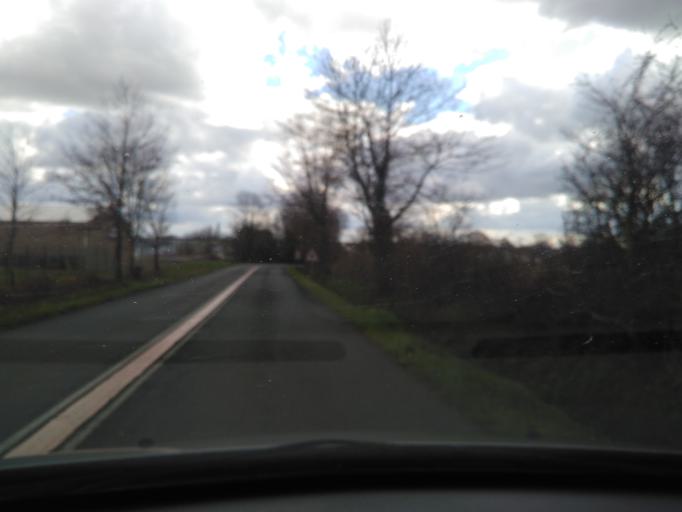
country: FR
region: Pays de la Loire
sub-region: Departement de la Vendee
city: Saint-Martin-des-Noyers
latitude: 46.7330
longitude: -1.1821
